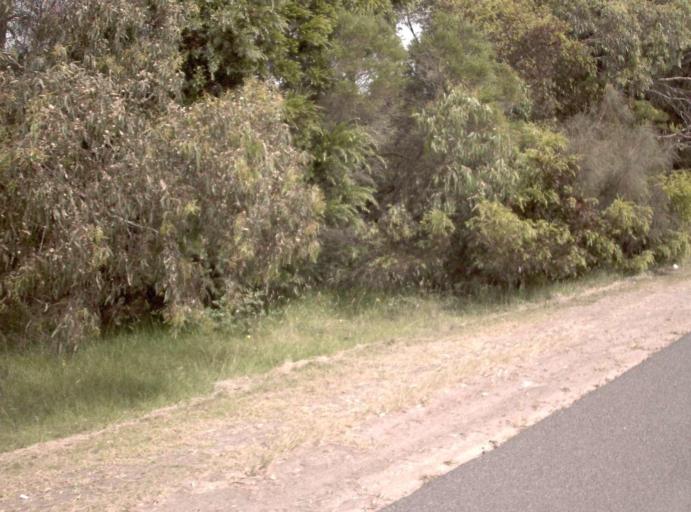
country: AU
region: Victoria
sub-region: Mornington Peninsula
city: Moorooduc
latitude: -38.2288
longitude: 145.0954
